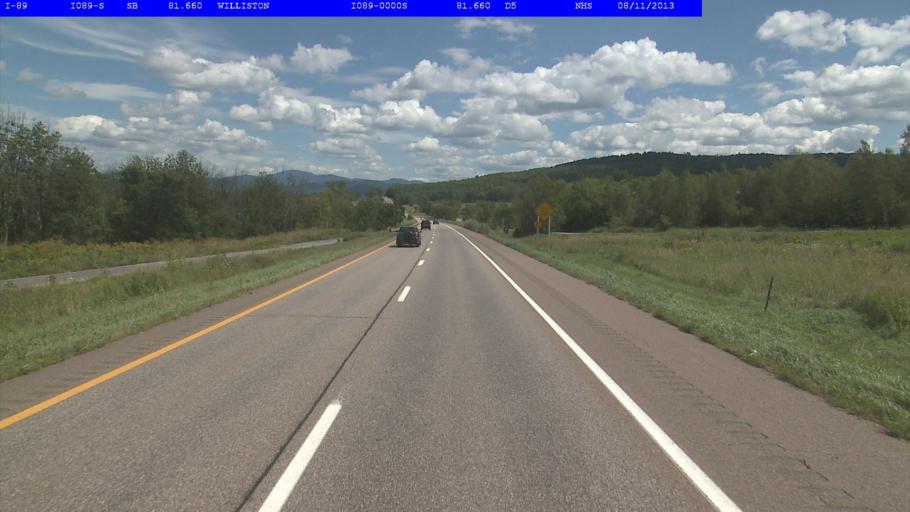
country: US
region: Vermont
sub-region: Chittenden County
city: Williston
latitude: 44.4337
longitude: -73.0695
